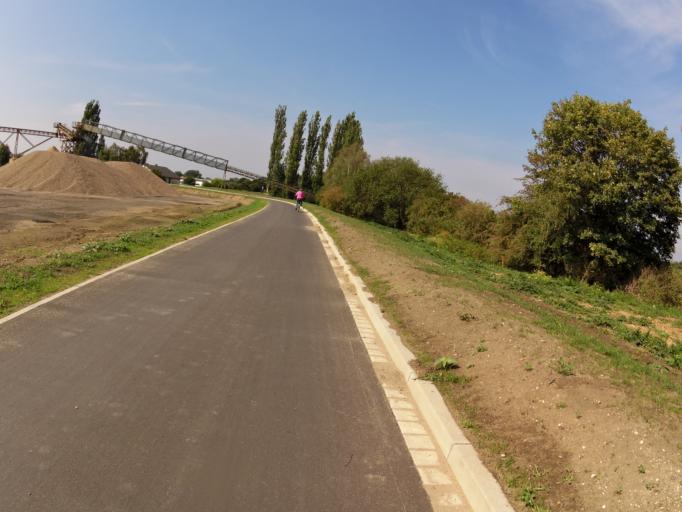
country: DE
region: Bremen
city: Bremen
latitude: 53.0239
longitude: 8.8712
